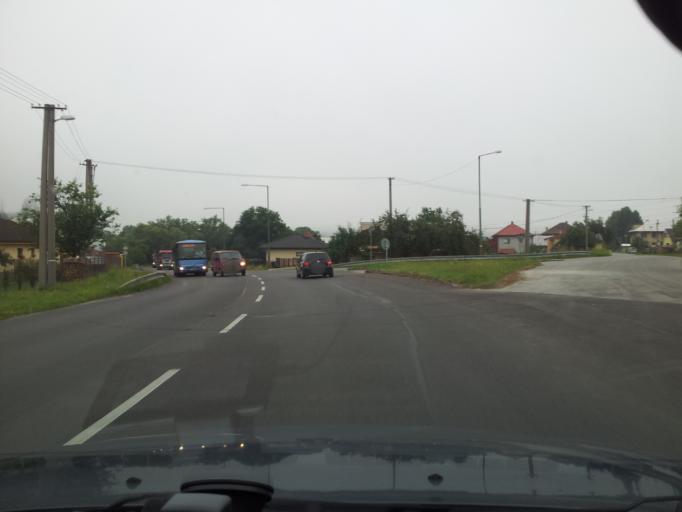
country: SK
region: Zilinsky
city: Cadca
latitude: 49.3983
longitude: 18.8503
